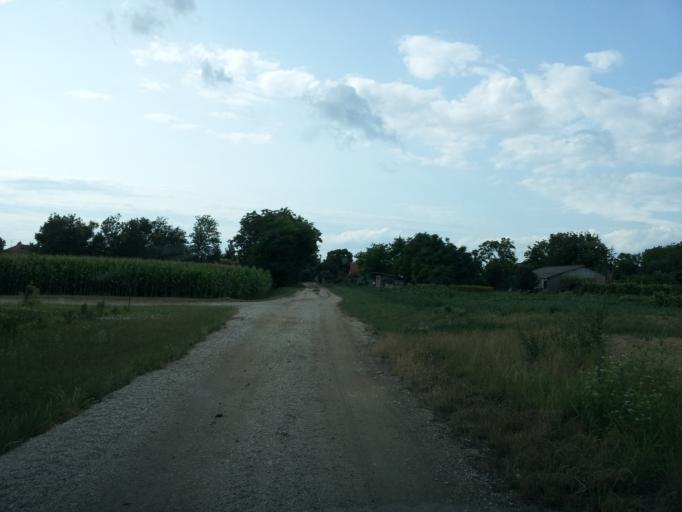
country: HU
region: Fejer
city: Lajoskomarom
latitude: 46.8442
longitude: 18.3504
